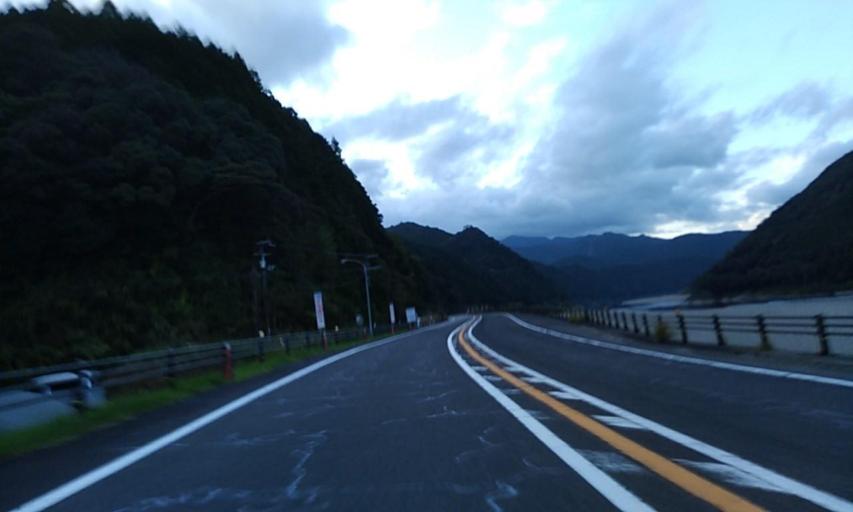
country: JP
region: Wakayama
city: Shingu
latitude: 33.7251
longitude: 135.9582
